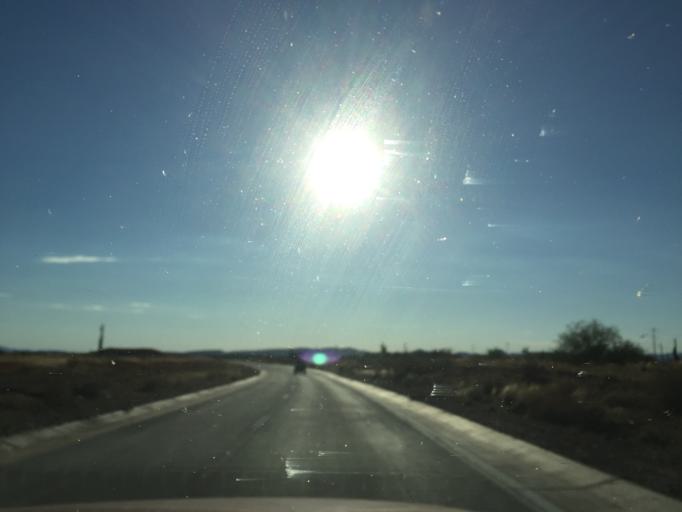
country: US
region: Arizona
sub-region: Maricopa County
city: Anthem
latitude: 33.7828
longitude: -112.1990
